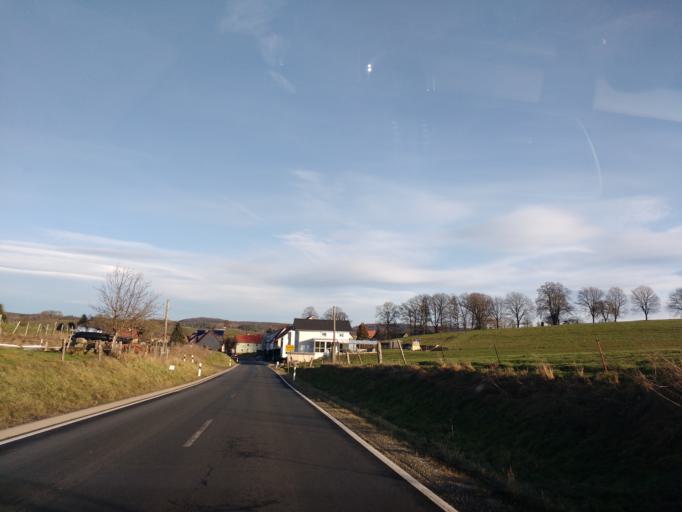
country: DE
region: Thuringia
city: Burgwalde
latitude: 51.3884
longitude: 10.0377
